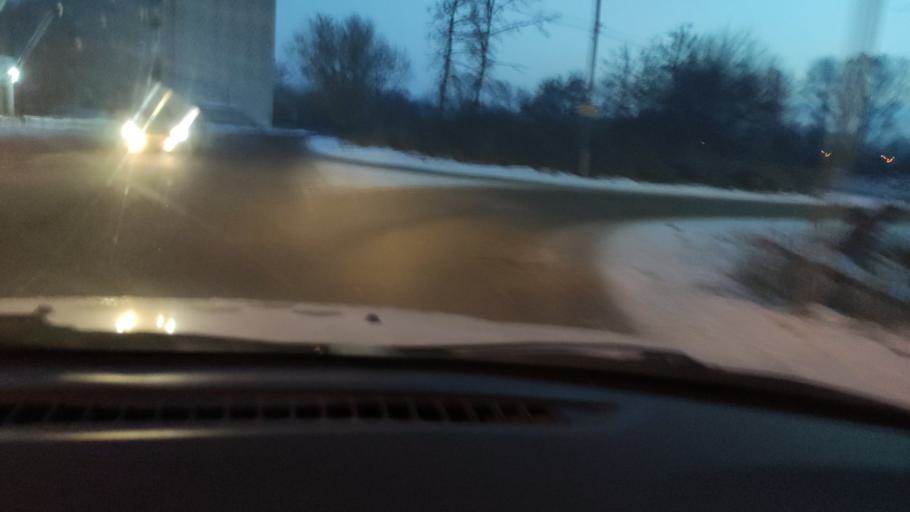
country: RU
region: Perm
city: Kungur
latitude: 57.4345
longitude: 56.9315
